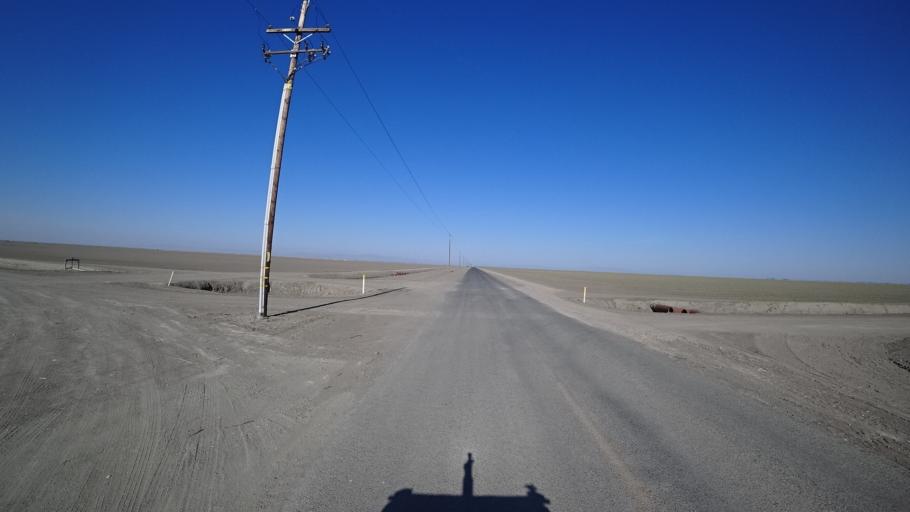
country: US
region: California
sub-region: Kings County
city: Stratford
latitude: 36.0797
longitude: -119.7155
